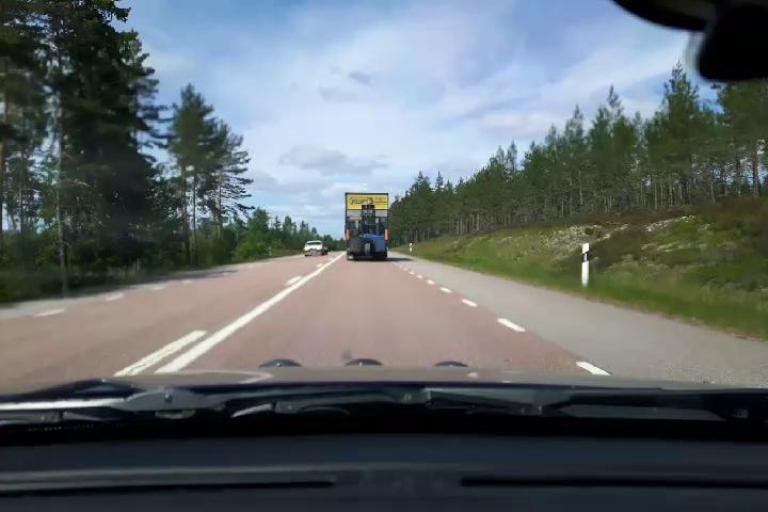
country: SE
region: Uppsala
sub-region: Osthammars Kommun
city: Bjorklinge
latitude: 60.1768
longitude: 17.4833
